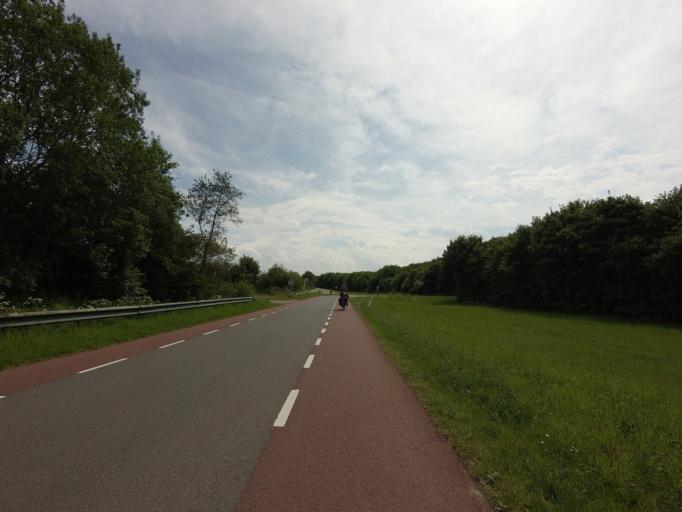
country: NL
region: North Brabant
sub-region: Gemeente Moerdijk
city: Willemstad
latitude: 51.7023
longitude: 4.3959
